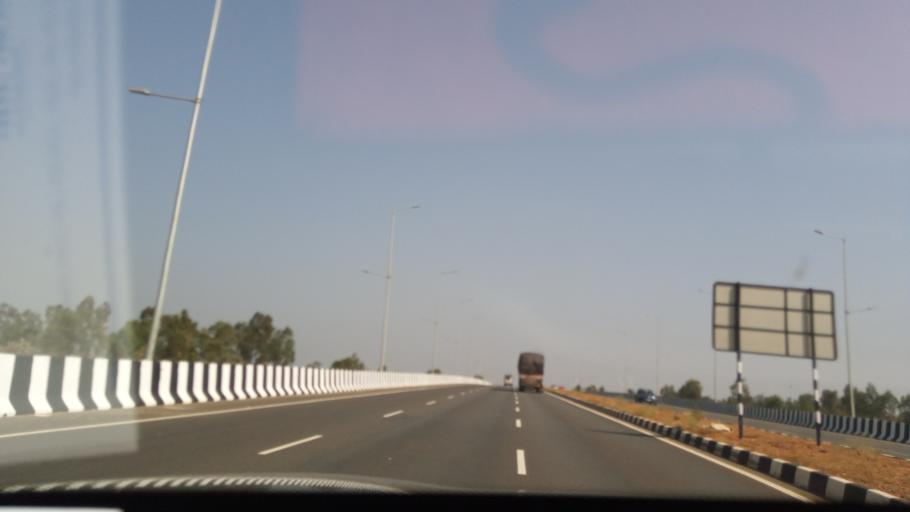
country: IN
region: Karnataka
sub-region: Haveri
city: Shiggaon
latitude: 15.0988
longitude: 75.1529
